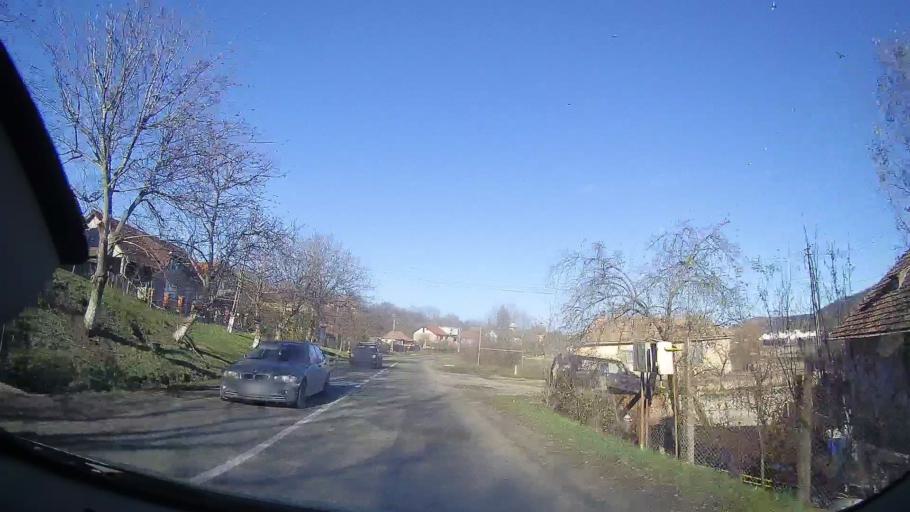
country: RO
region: Mures
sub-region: Comuna Sarmasu
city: Sarmasu
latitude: 46.7804
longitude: 24.2026
